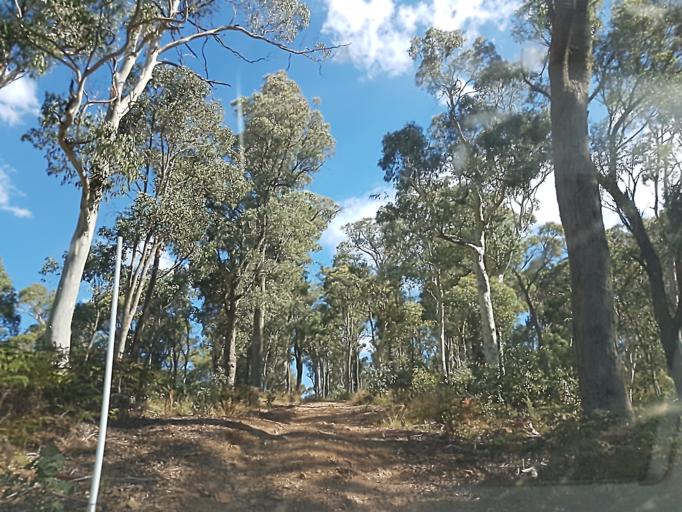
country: AU
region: Victoria
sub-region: Alpine
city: Mount Beauty
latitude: -36.8819
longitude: 147.0240
